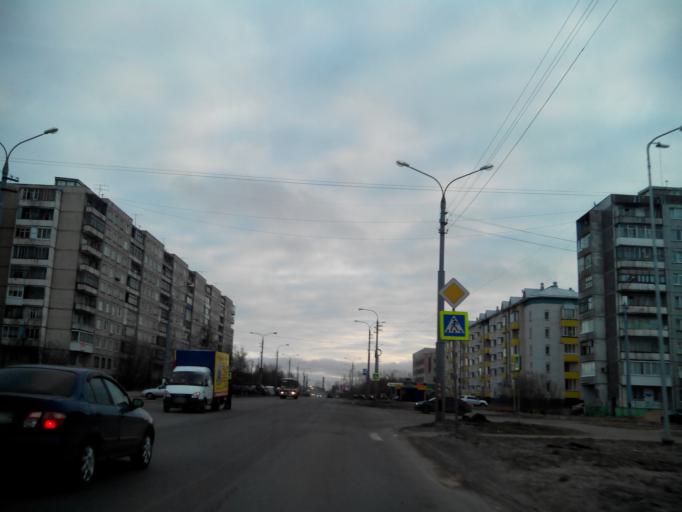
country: RU
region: Arkhangelskaya
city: Arkhangel'sk
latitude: 64.5153
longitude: 40.6712
